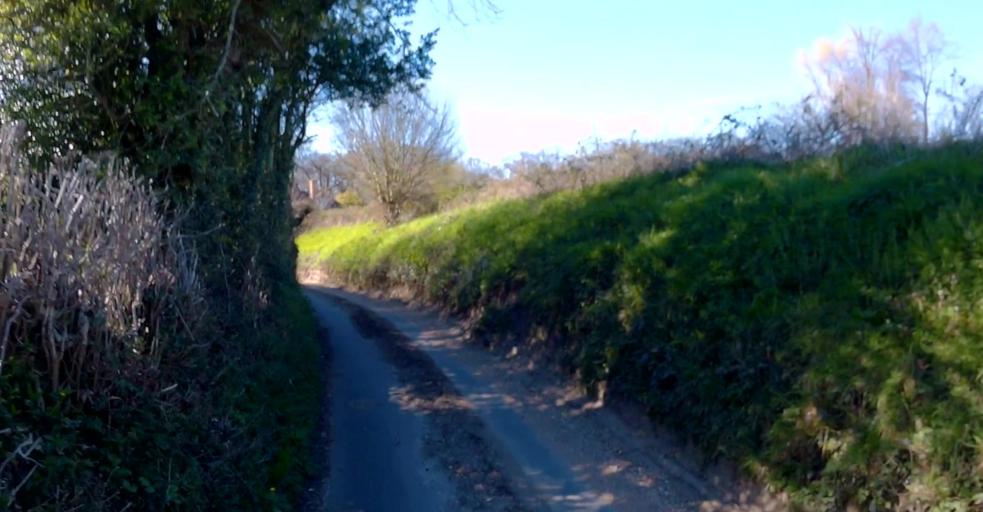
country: GB
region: England
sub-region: Surrey
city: Farnham
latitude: 51.2136
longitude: -0.8397
